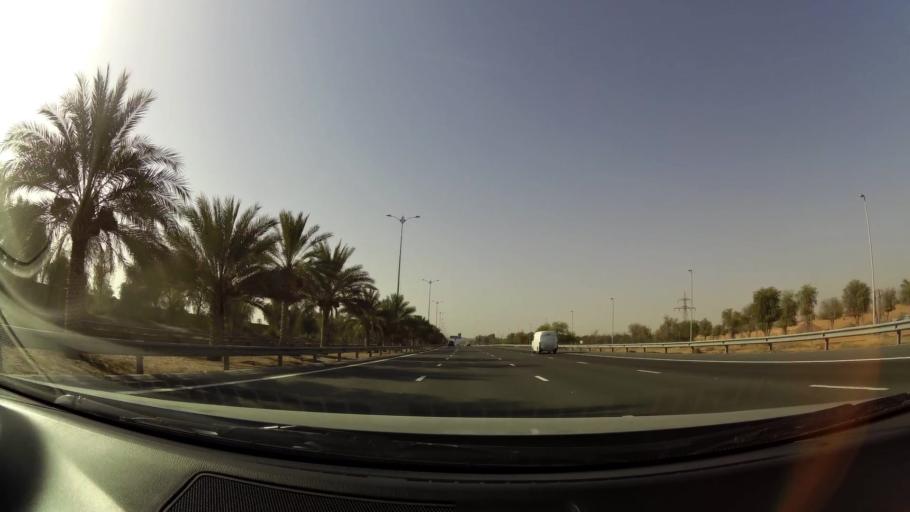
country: OM
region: Al Buraimi
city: Al Buraymi
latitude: 24.6004
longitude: 55.7330
